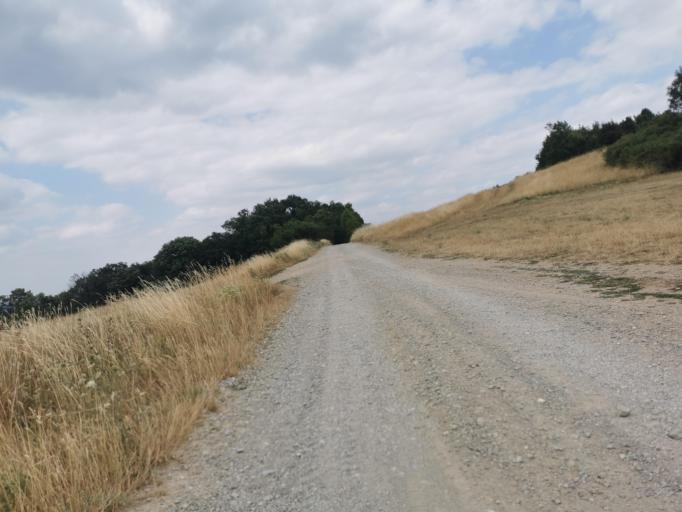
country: SK
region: Nitriansky
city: Brezova pod Bradlom
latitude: 48.6838
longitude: 17.5043
